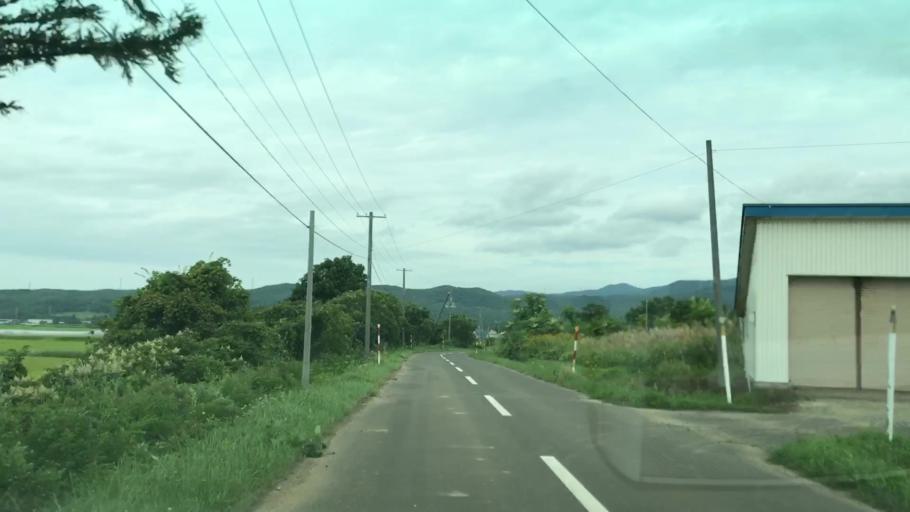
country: JP
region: Hokkaido
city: Iwanai
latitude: 43.0252
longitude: 140.5698
